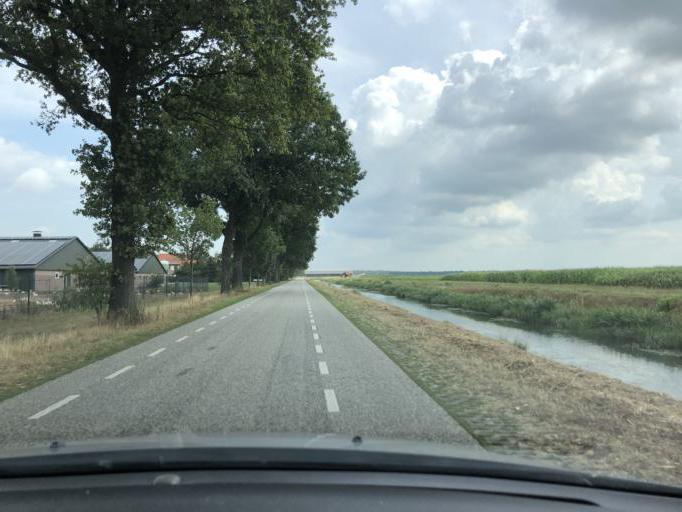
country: NL
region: Drenthe
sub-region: Gemeente Coevorden
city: Dalen
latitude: 52.7909
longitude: 6.6374
